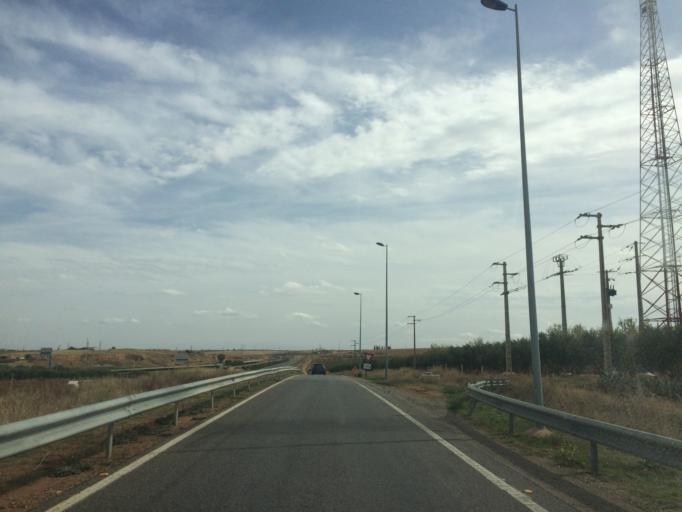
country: MA
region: Meknes-Tafilalet
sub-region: Meknes
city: Meknes
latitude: 33.8318
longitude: -5.5686
